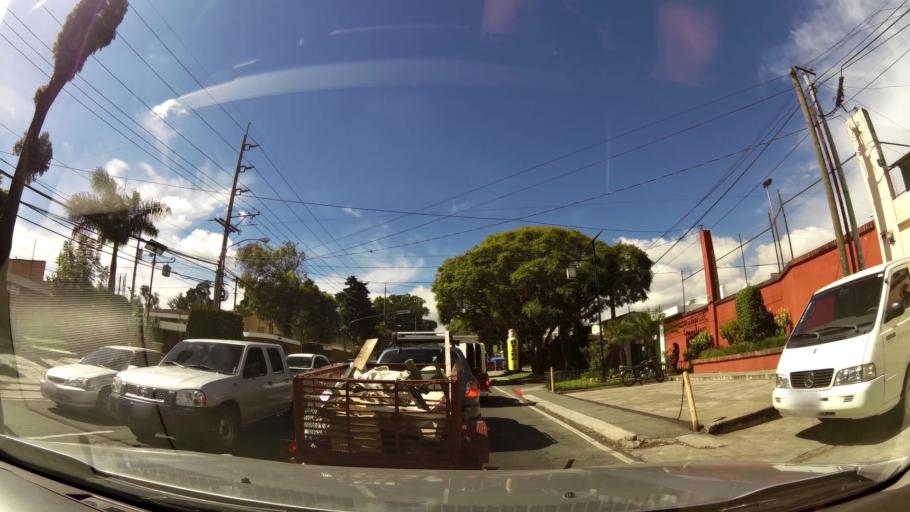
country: GT
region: Guatemala
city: Mixco
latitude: 14.6318
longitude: -90.5610
